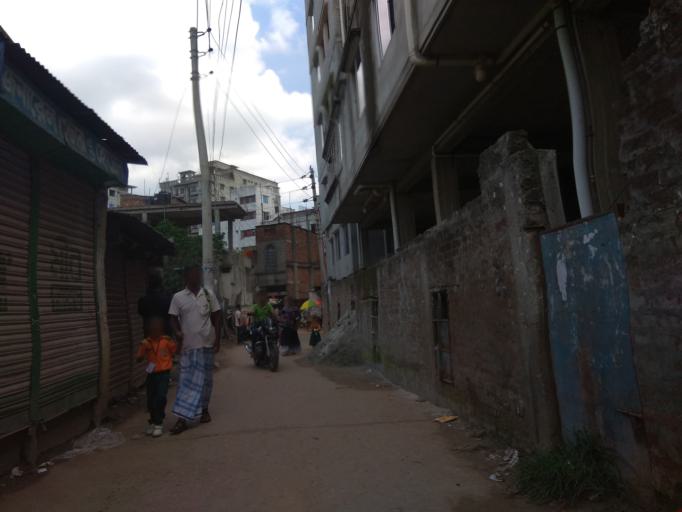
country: BD
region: Dhaka
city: Tungi
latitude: 23.8270
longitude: 90.3914
